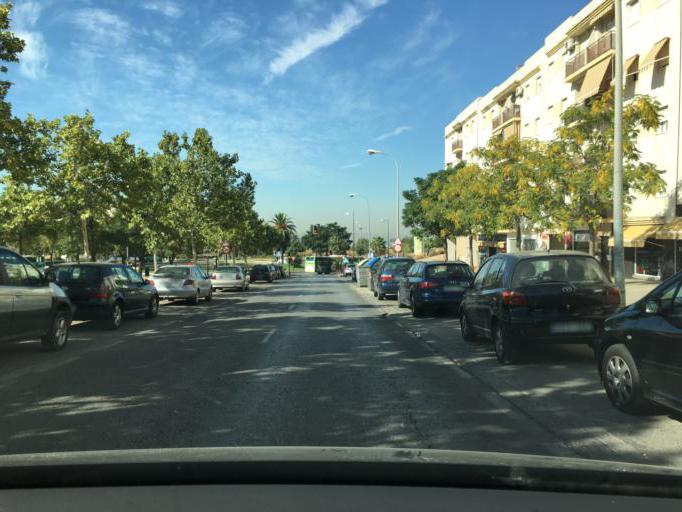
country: ES
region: Andalusia
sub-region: Provincia de Granada
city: Maracena
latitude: 37.2072
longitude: -3.6183
